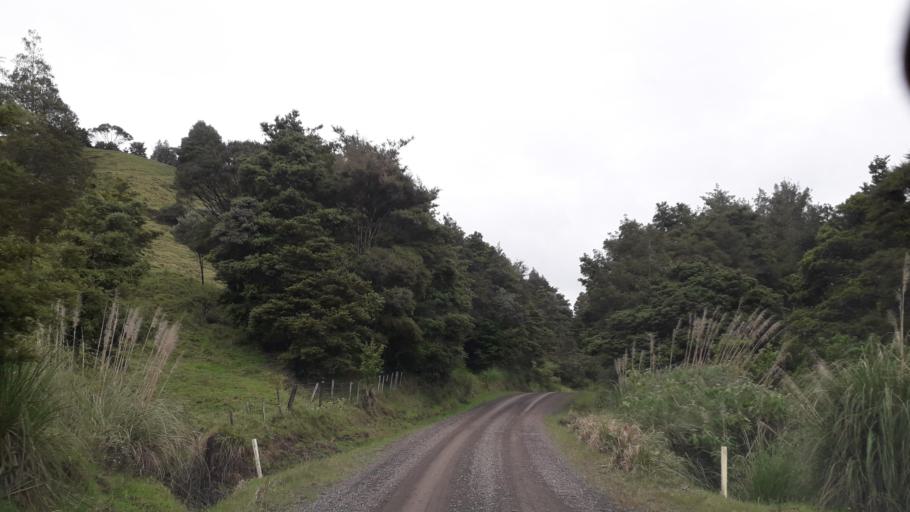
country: NZ
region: Northland
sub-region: Far North District
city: Kaitaia
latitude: -35.3825
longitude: 173.4099
